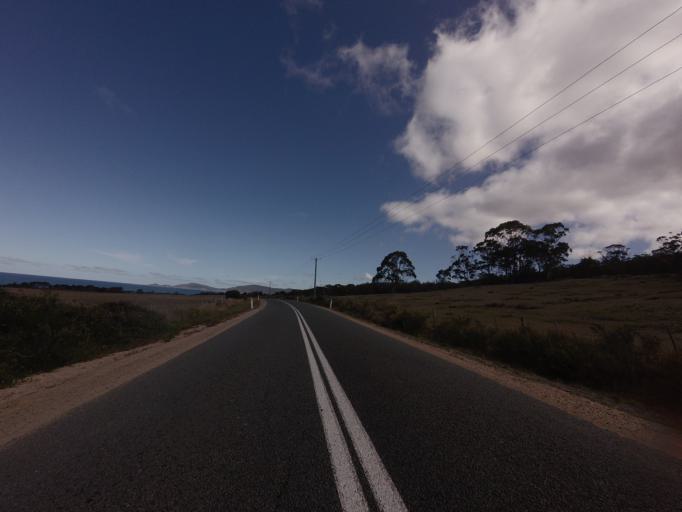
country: AU
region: Tasmania
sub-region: Break O'Day
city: St Helens
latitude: -41.7889
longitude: 148.2619
